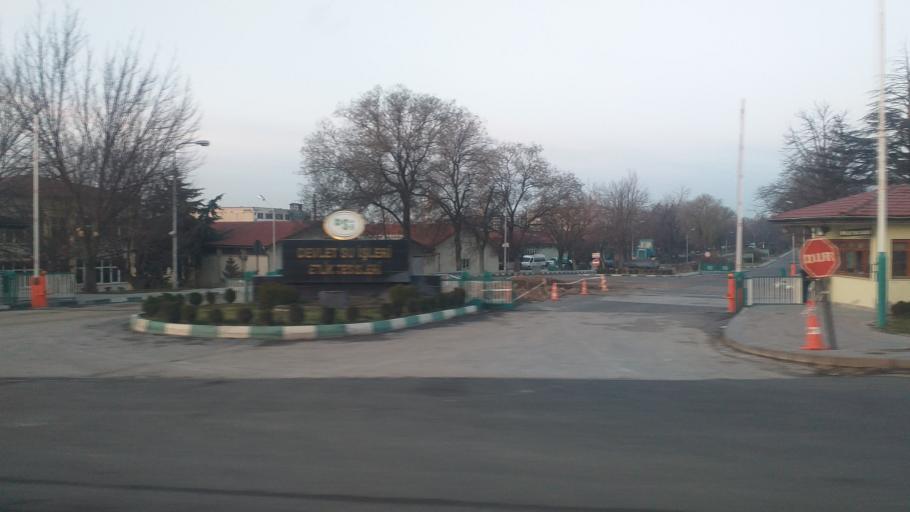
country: TR
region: Ankara
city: Ankara
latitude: 39.9611
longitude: 32.8459
